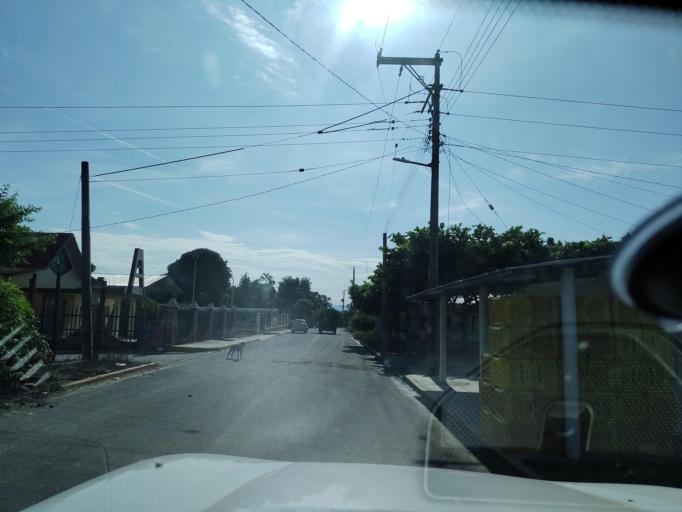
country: MX
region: Veracruz
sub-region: Martinez de la Torre
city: El Progreso
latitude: 20.1115
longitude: -96.9877
